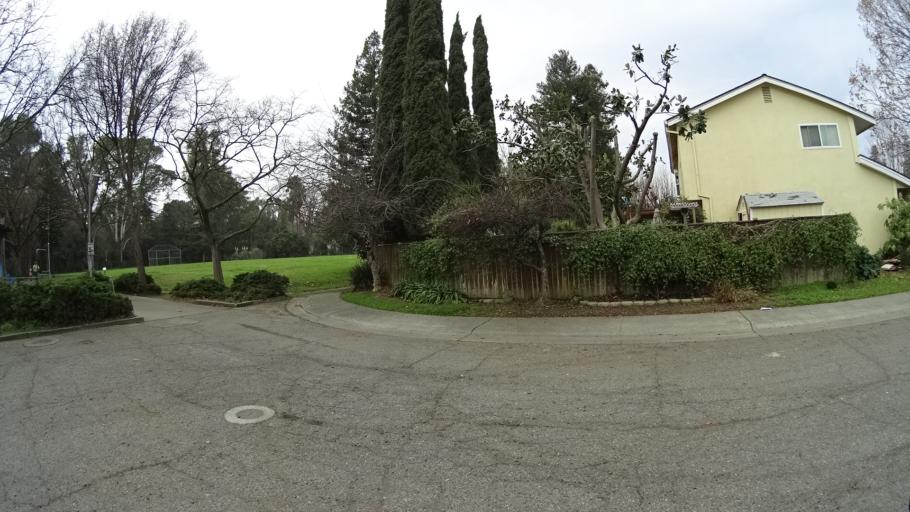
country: US
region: California
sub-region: Yolo County
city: Davis
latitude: 38.5427
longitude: -121.7092
